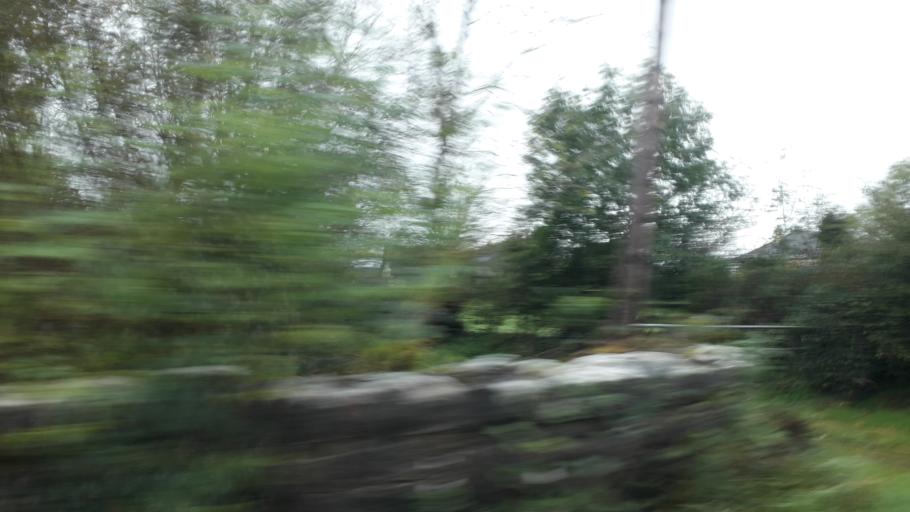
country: IE
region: Connaught
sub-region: Roscommon
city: Ballaghaderreen
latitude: 53.8915
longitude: -8.5512
